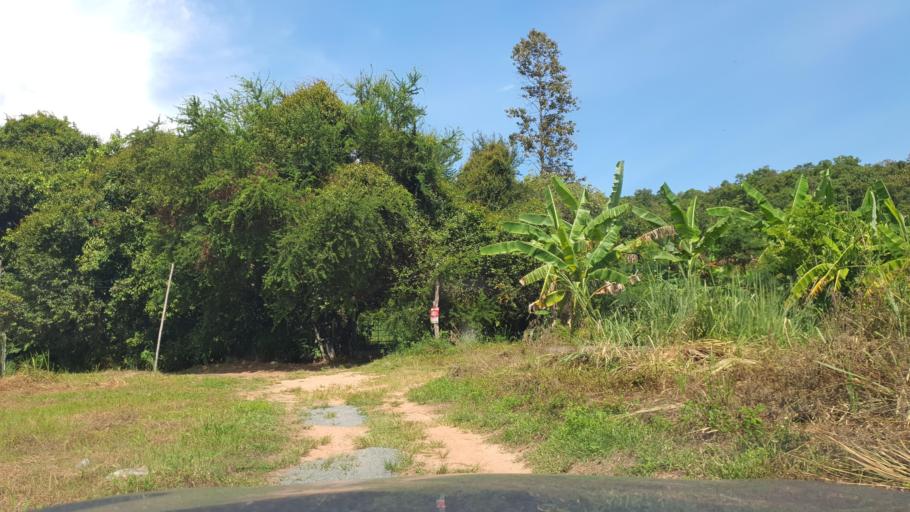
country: TH
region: Chiang Mai
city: Mae On
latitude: 18.7786
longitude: 99.1885
